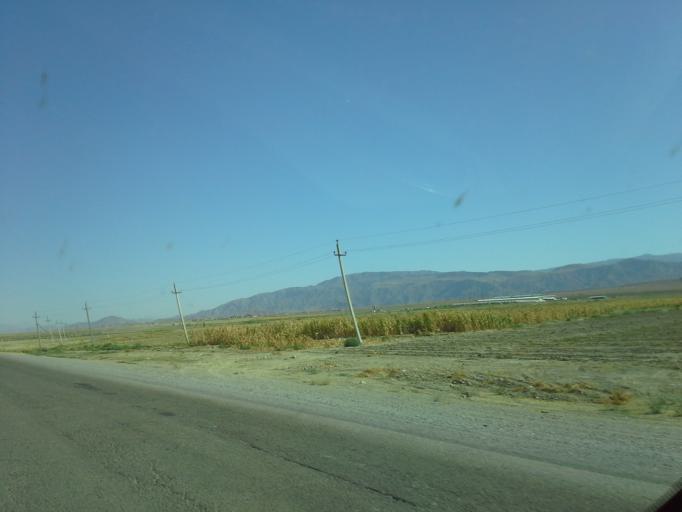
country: TM
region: Ahal
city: Baharly
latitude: 38.4562
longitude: 57.3637
